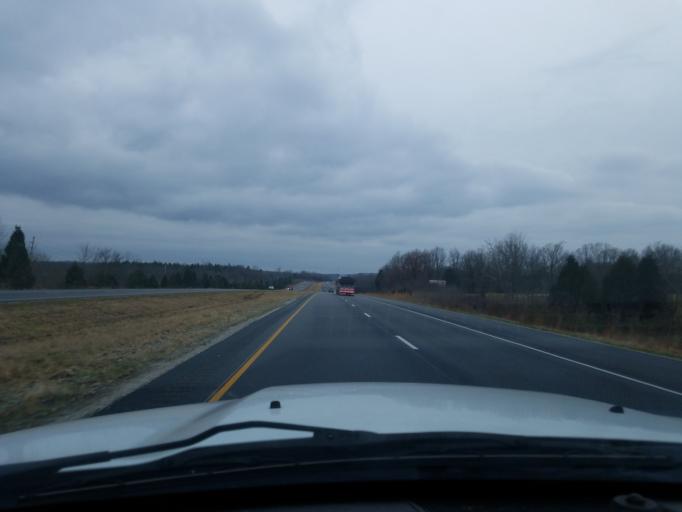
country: US
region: Indiana
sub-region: Crawford County
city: English
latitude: 38.2452
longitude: -86.4303
